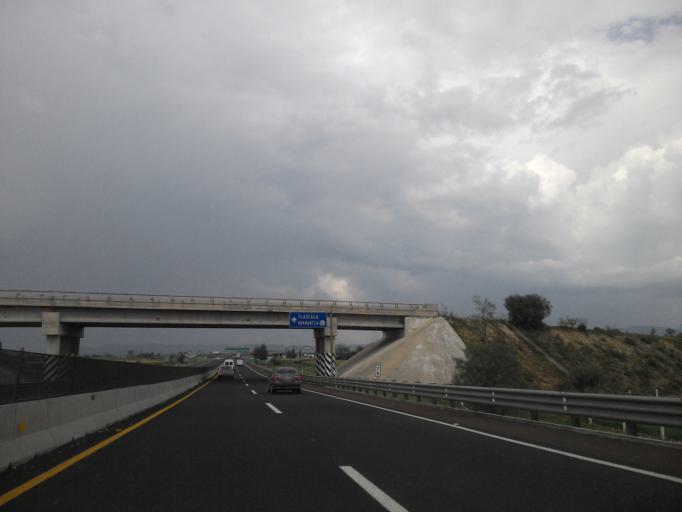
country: MX
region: Hidalgo
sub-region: Tula de Allende
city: Residencial Arboledas
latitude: 20.0971
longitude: -99.2915
